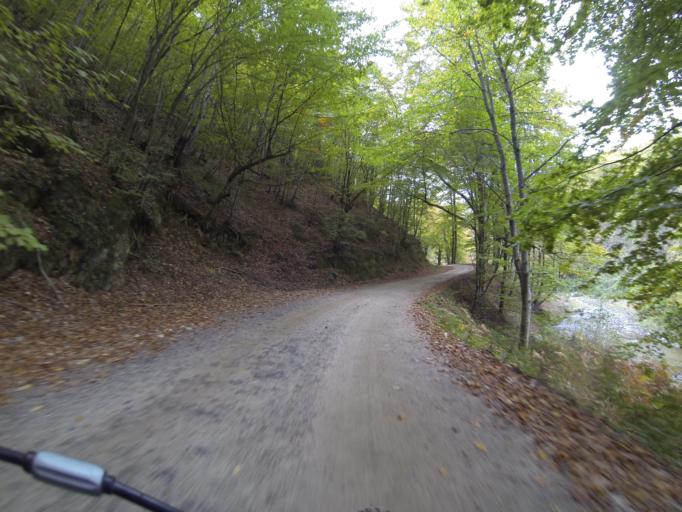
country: RO
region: Gorj
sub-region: Comuna Tismana
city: Sohodol
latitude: 45.0619
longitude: 22.8970
